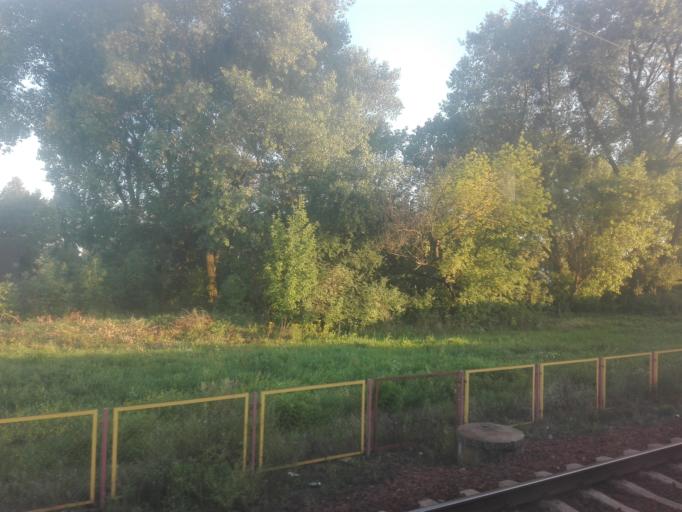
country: PL
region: Masovian Voivodeship
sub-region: Powiat warszawski zachodni
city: Jozefow
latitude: 52.2001
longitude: 20.7031
